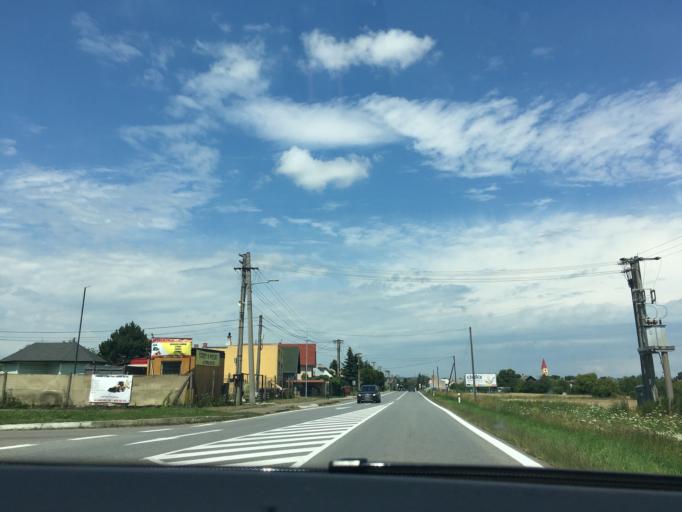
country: SK
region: Presovsky
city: Vranov nad Topl'ou
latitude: 48.8160
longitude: 21.6866
